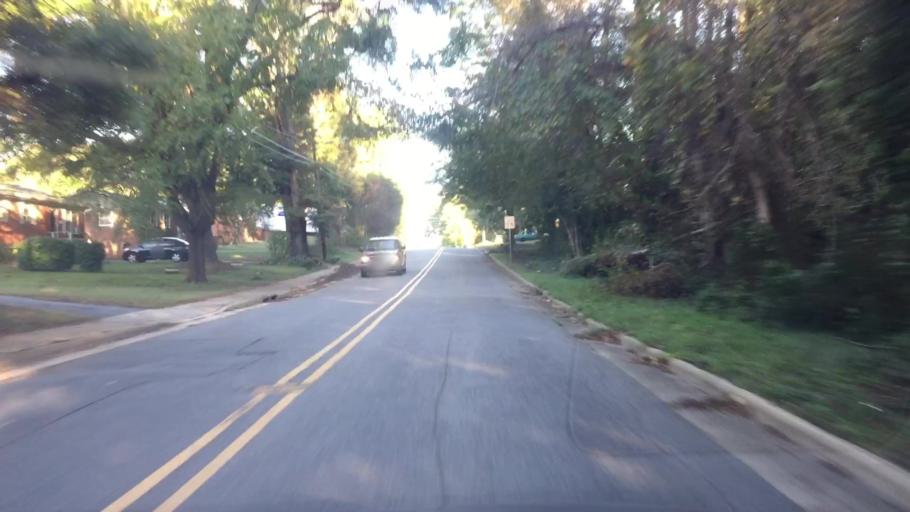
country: US
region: North Carolina
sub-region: Iredell County
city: Mooresville
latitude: 35.5759
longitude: -80.8085
